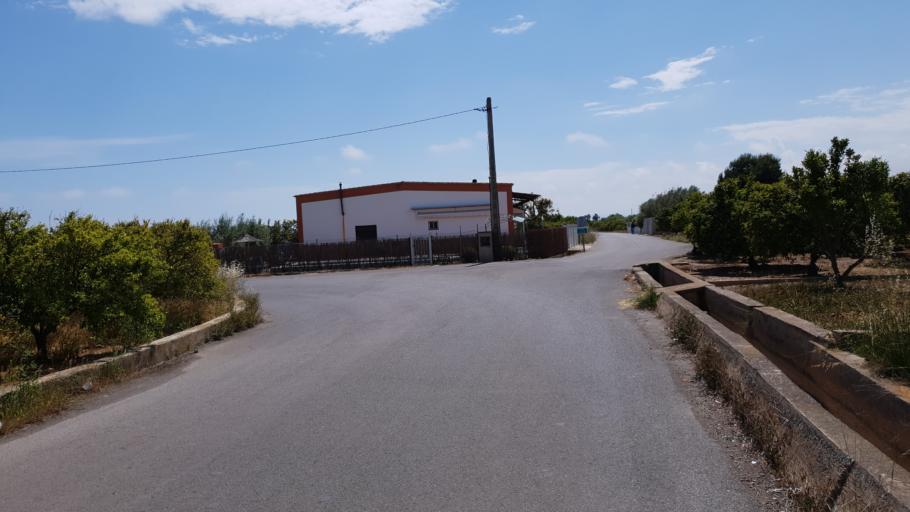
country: ES
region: Valencia
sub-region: Provincia de Castello
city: Burriana
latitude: 39.8610
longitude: -0.0898
